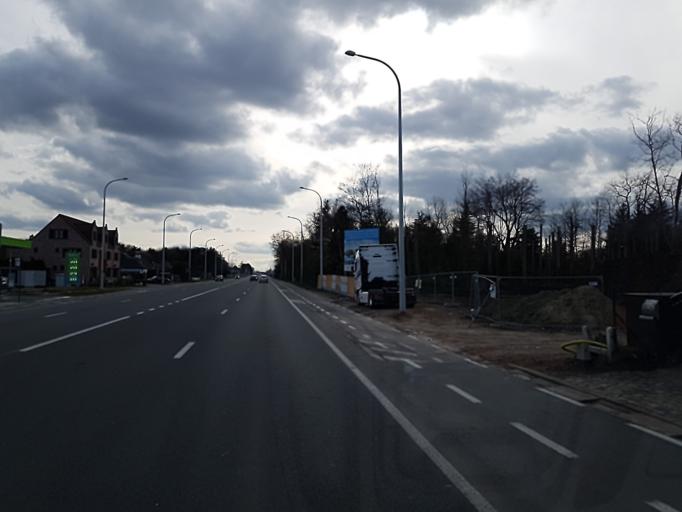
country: BE
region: Flanders
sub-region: Provincie Oost-Vlaanderen
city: Sint-Niklaas
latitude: 51.1768
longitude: 4.1908
